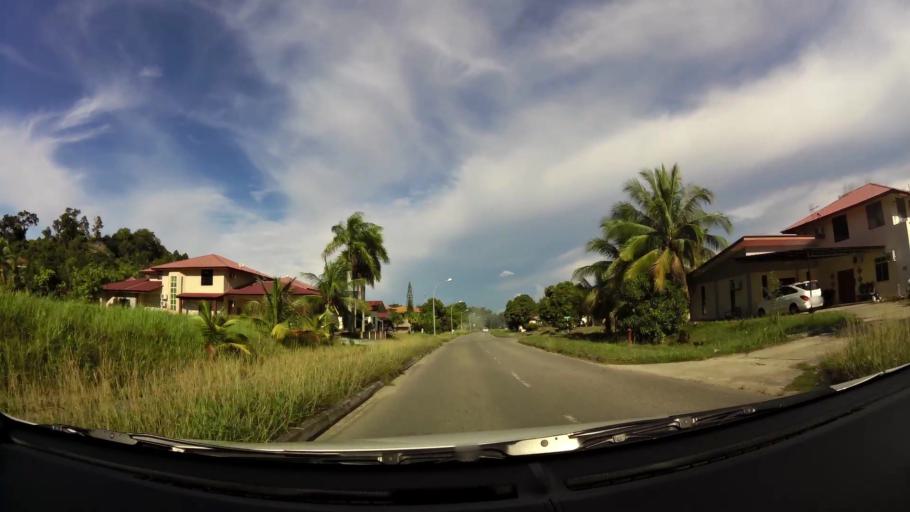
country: BN
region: Brunei and Muara
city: Bandar Seri Begawan
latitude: 4.9700
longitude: 114.9618
